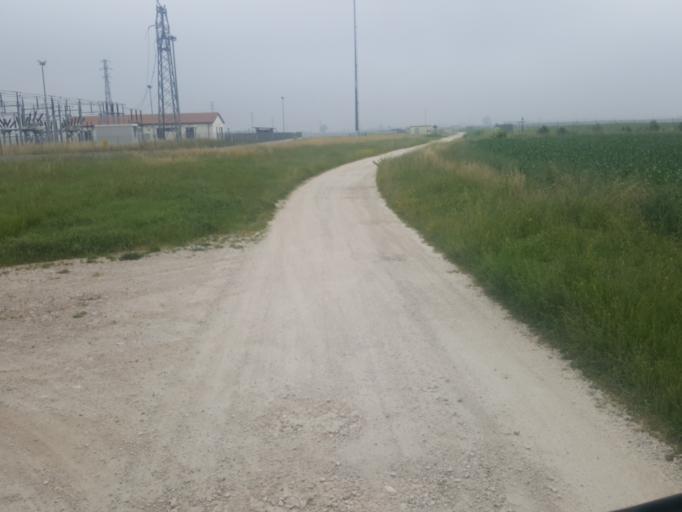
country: IT
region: Veneto
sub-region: Provincia di Rovigo
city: Canaro
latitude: 44.9397
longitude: 11.6495
